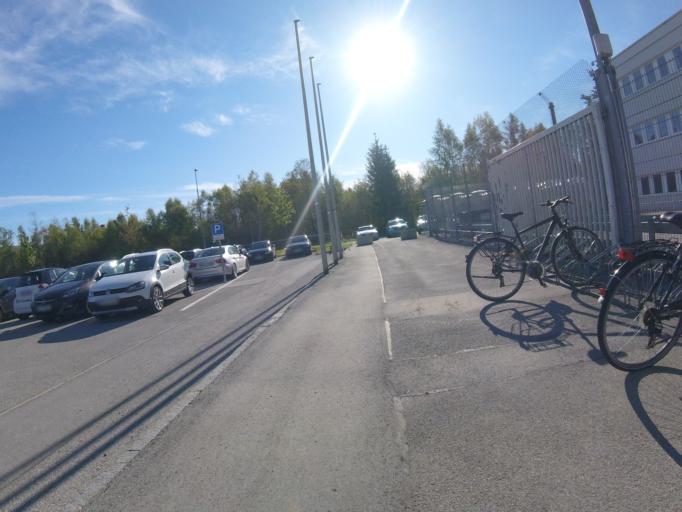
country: DE
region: Bavaria
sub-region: Upper Bavaria
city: Ottobrunn
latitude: 48.0479
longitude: 11.6573
